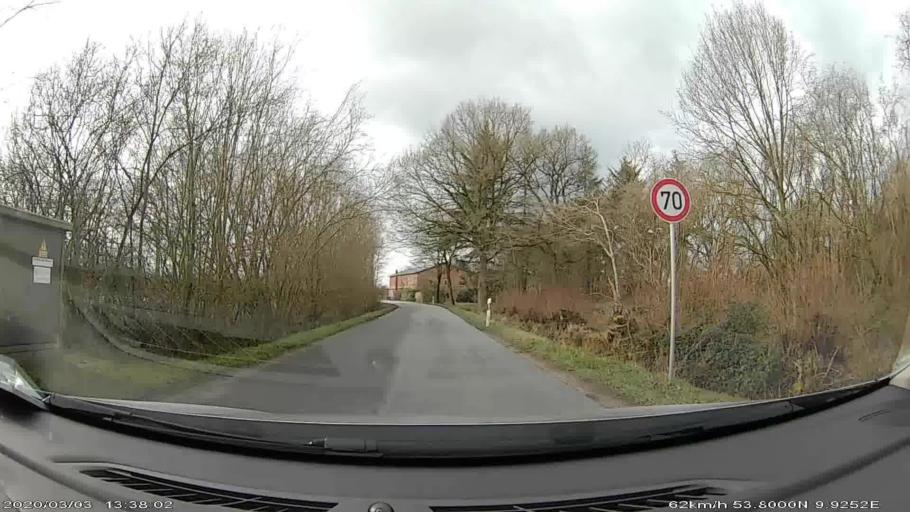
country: DE
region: Schleswig-Holstein
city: Alveslohe
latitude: 53.8003
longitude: 9.9239
